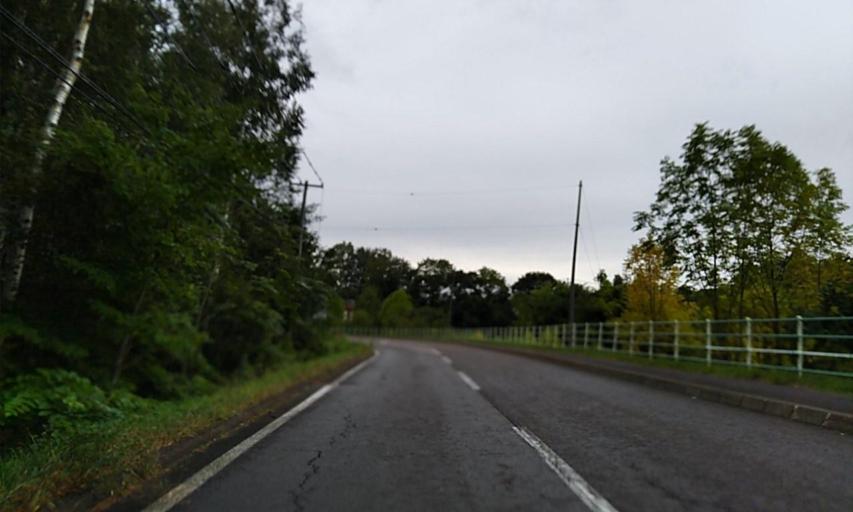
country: JP
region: Hokkaido
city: Abashiri
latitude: 43.9990
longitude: 144.2290
